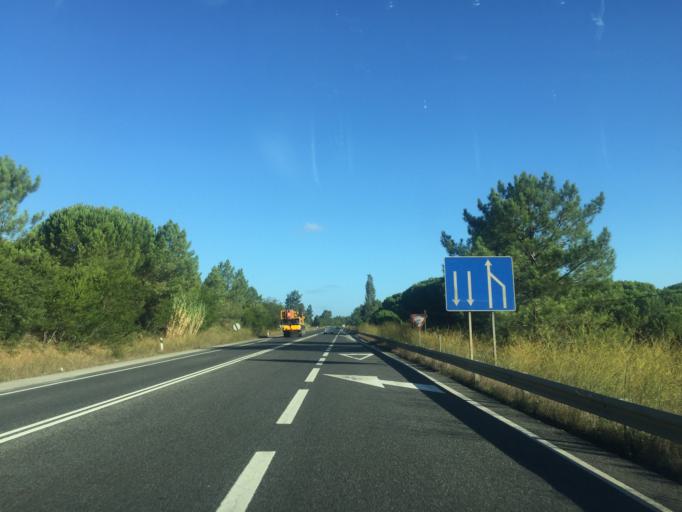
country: PT
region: Lisbon
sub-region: Azambuja
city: Alcoentre
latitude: 39.2524
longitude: -8.9522
